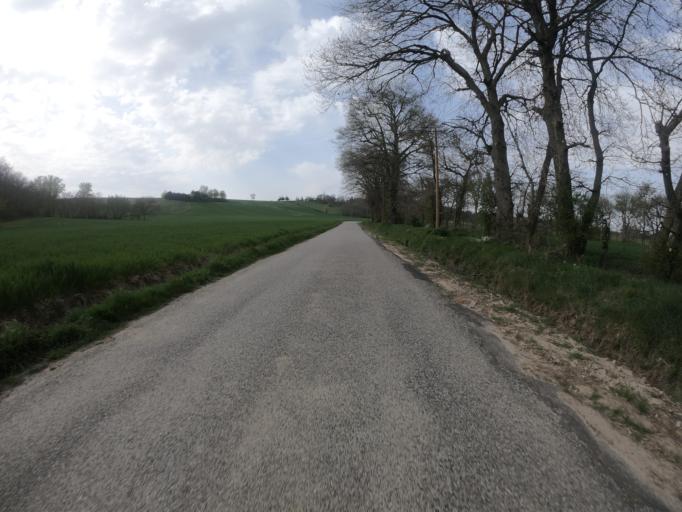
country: FR
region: Midi-Pyrenees
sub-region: Departement de l'Ariege
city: La Tour-du-Crieu
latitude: 43.1312
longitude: 1.7160
